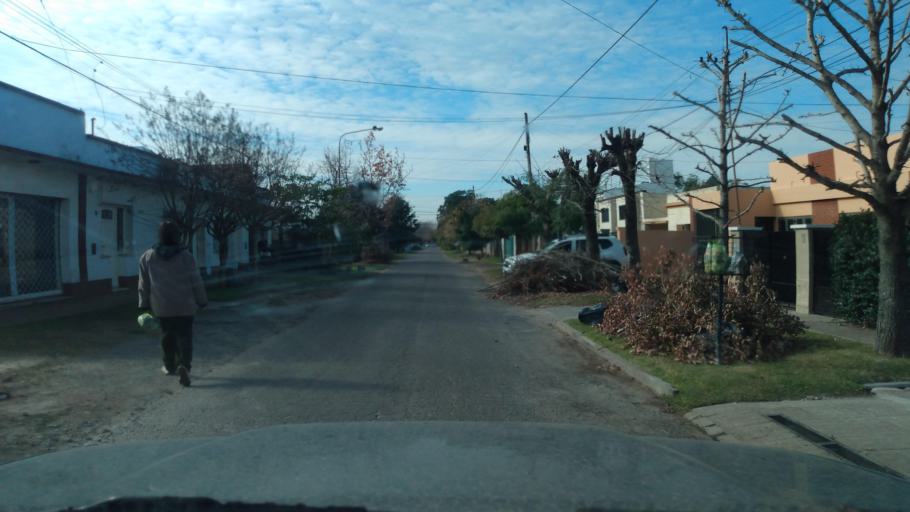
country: AR
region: Buenos Aires
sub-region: Partido de Lujan
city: Lujan
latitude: -34.5970
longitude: -59.1801
